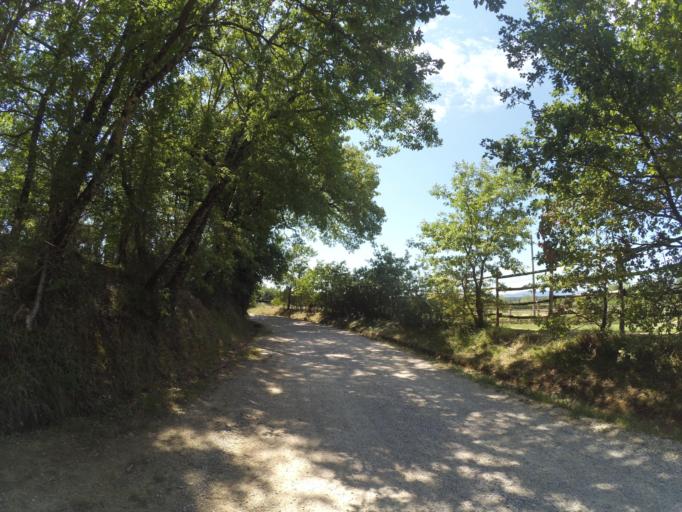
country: IT
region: Tuscany
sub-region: Province of Arezzo
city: Castiglion Fibocchi
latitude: 43.5342
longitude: 11.7654
